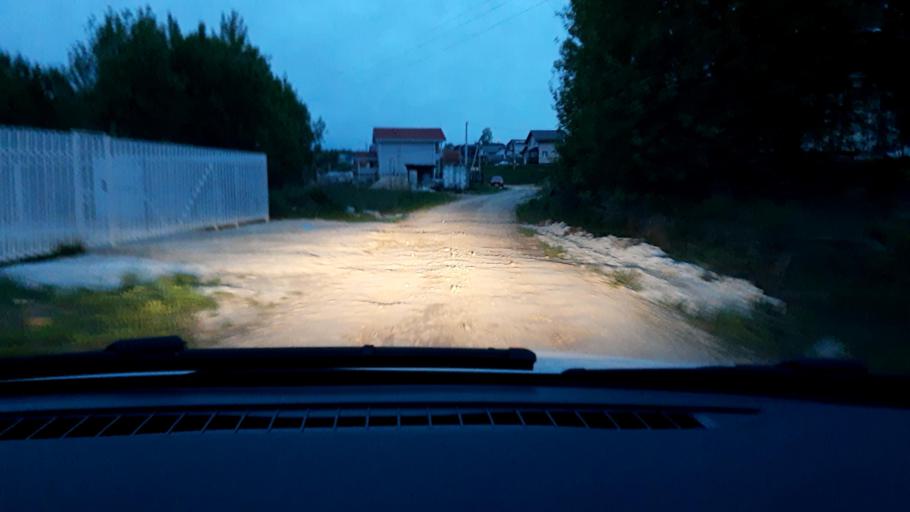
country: RU
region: Nizjnij Novgorod
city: Afonino
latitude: 56.2595
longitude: 44.0790
